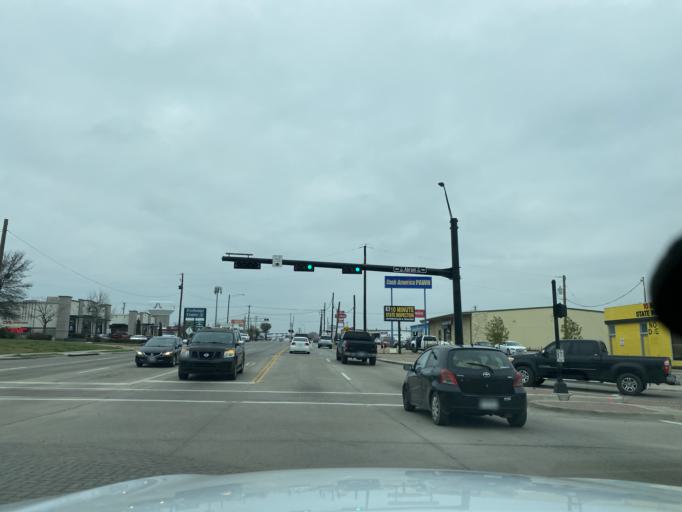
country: US
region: Texas
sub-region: Tarrant County
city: Arlington
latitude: 32.7356
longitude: -97.0973
